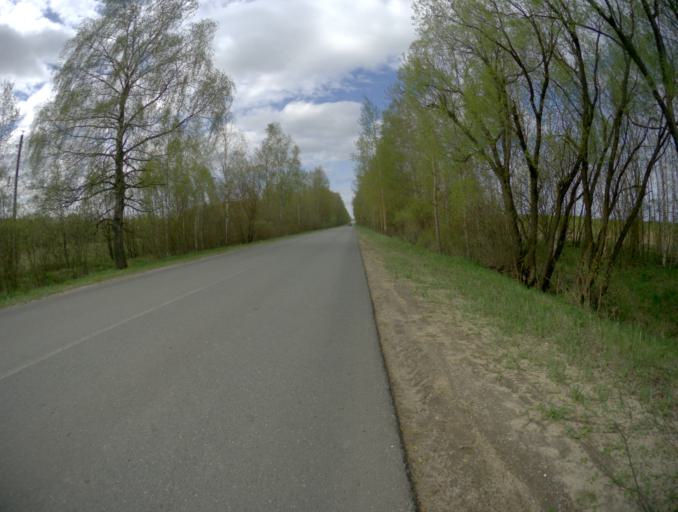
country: RU
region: Vladimir
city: Golovino
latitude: 55.9575
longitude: 40.4680
